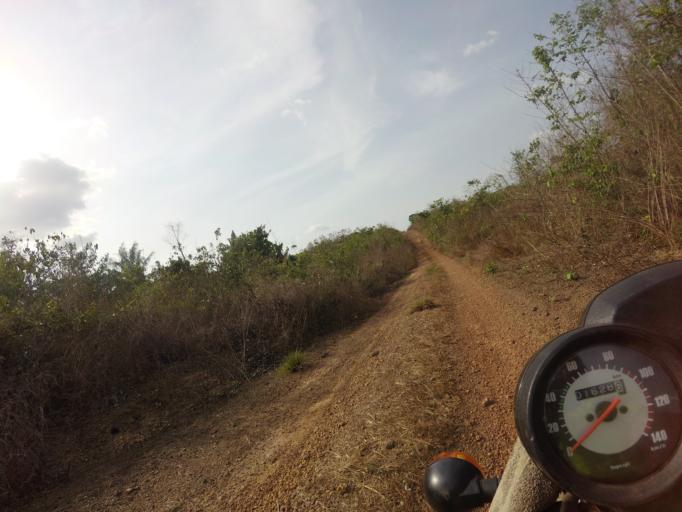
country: SL
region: Southern Province
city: Zimmi
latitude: 7.2391
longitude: -11.1810
